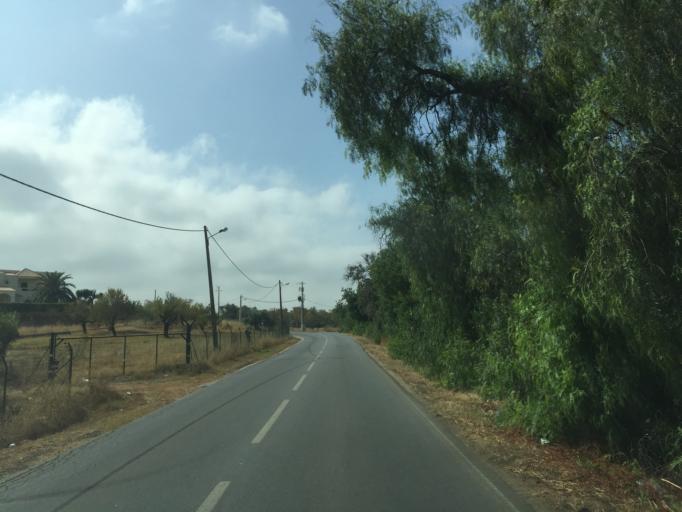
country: PT
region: Faro
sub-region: Olhao
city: Olhao
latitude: 37.0799
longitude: -7.8910
